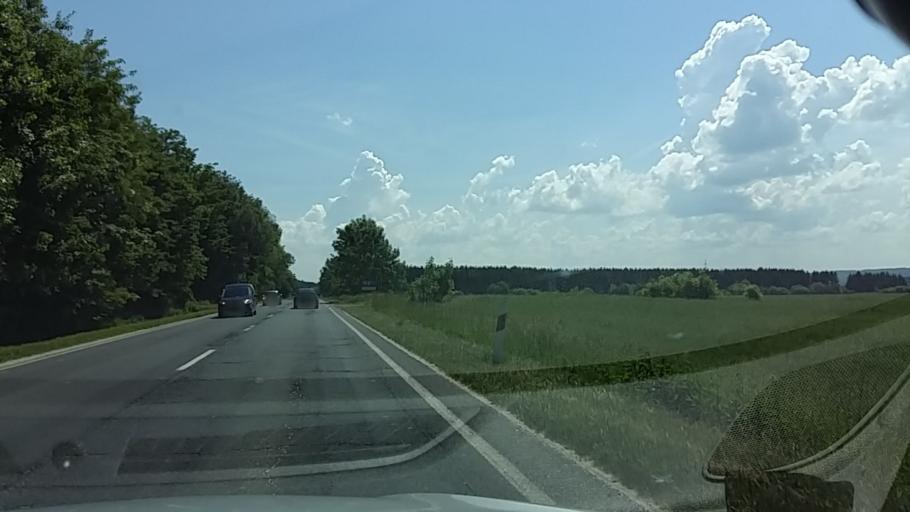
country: AT
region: Burgenland
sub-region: Politischer Bezirk Gussing
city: Inzenhof
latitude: 46.9800
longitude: 16.3162
